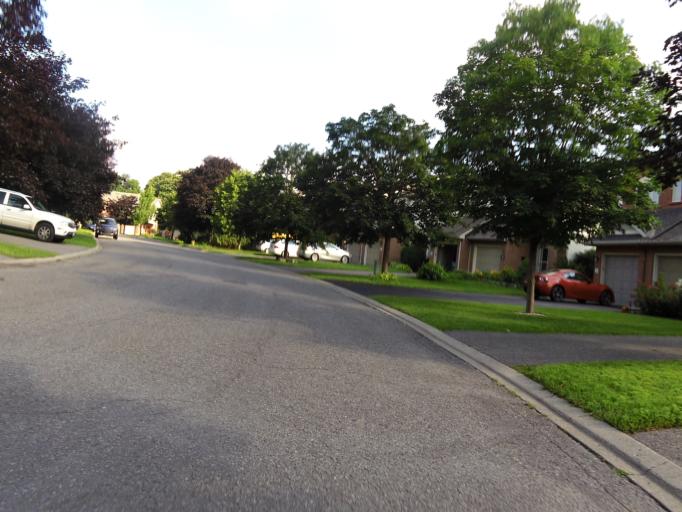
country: CA
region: Ontario
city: Ottawa
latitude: 45.3489
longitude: -75.6807
